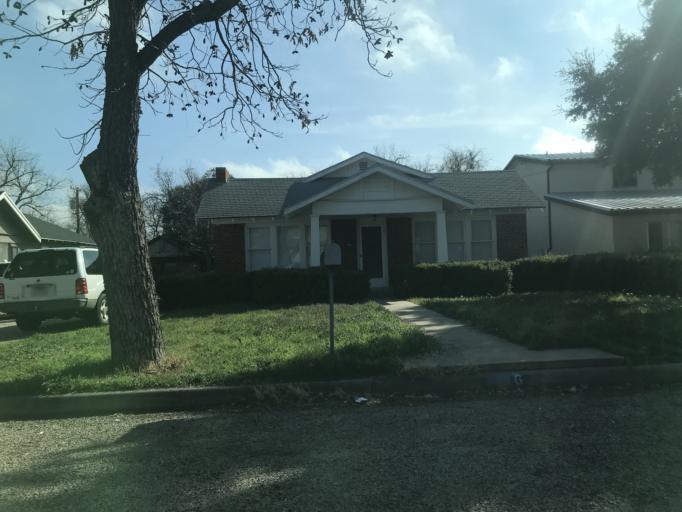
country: US
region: Texas
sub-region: Tom Green County
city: San Angelo
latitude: 31.4468
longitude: -100.4598
